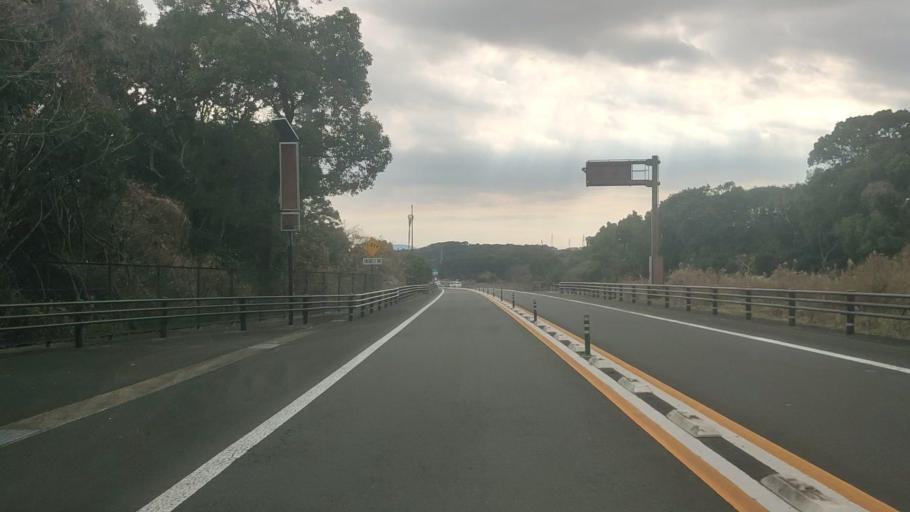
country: JP
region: Nagasaki
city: Shimabara
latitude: 32.7700
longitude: 130.3581
